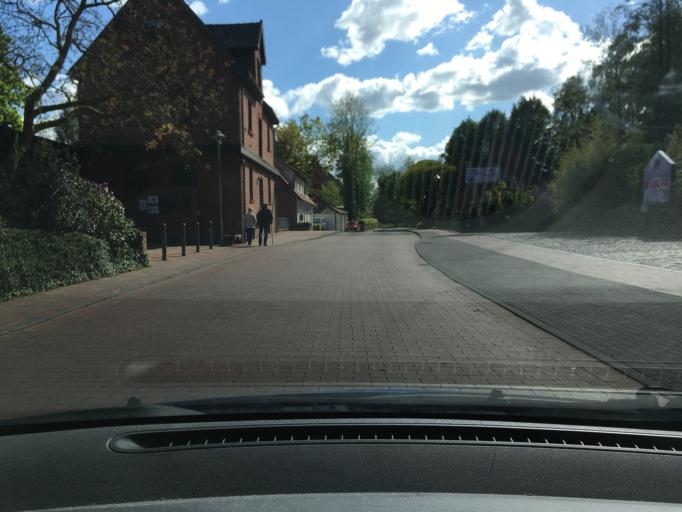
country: DE
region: Lower Saxony
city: Soltau
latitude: 52.9908
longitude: 9.8413
